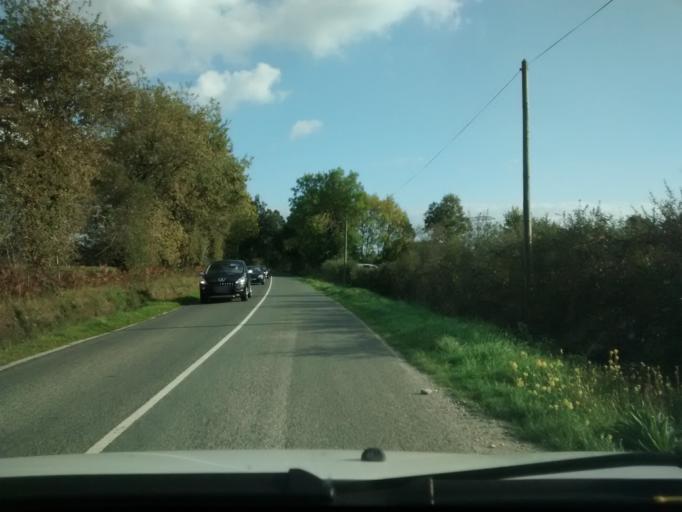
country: FR
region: Pays de la Loire
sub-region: Departement de la Loire-Atlantique
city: Sautron
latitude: 47.2846
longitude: -1.6520
